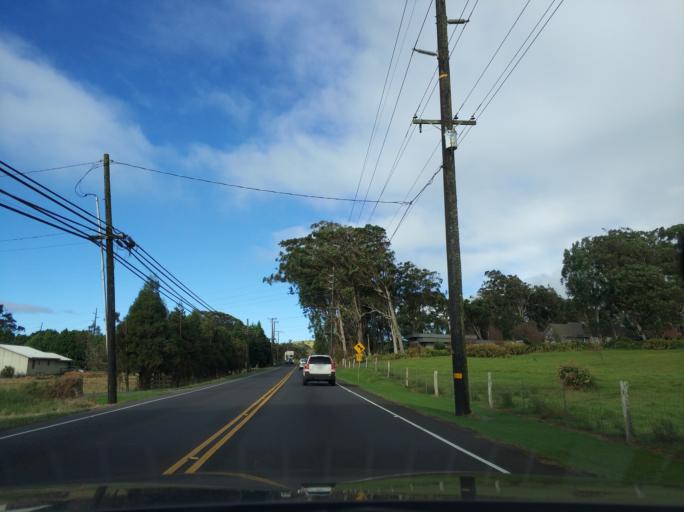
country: US
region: Hawaii
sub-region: Hawaii County
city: Waimea
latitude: 20.0352
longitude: -155.6309
